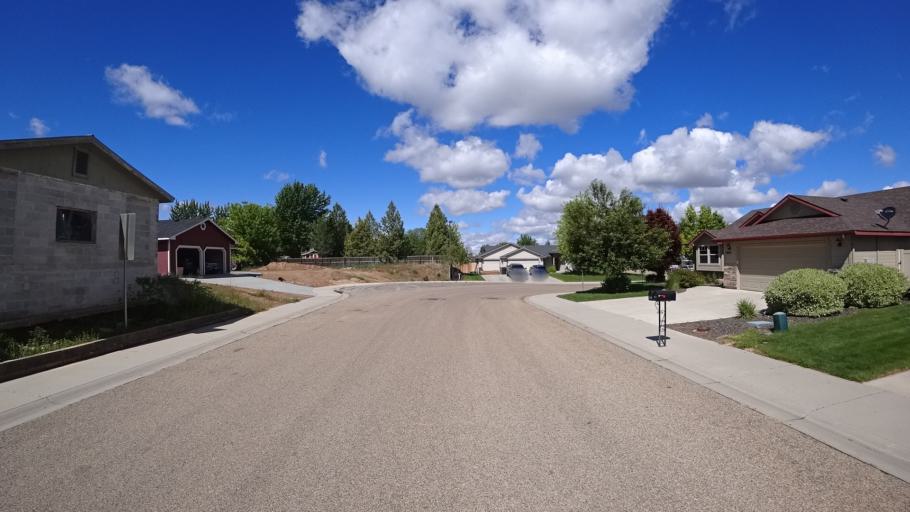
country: US
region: Idaho
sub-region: Ada County
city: Kuna
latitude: 43.4956
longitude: -116.4347
